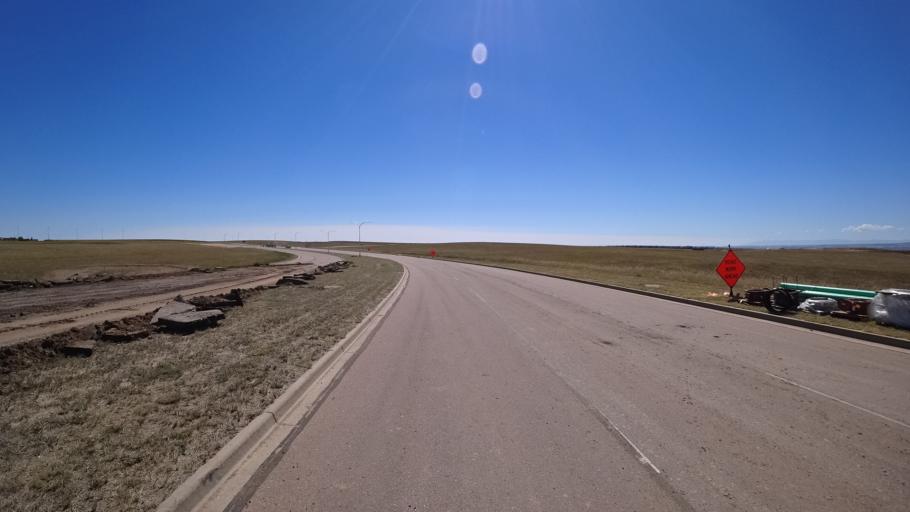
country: US
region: Colorado
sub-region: El Paso County
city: Security-Widefield
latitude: 38.7784
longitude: -104.7098
